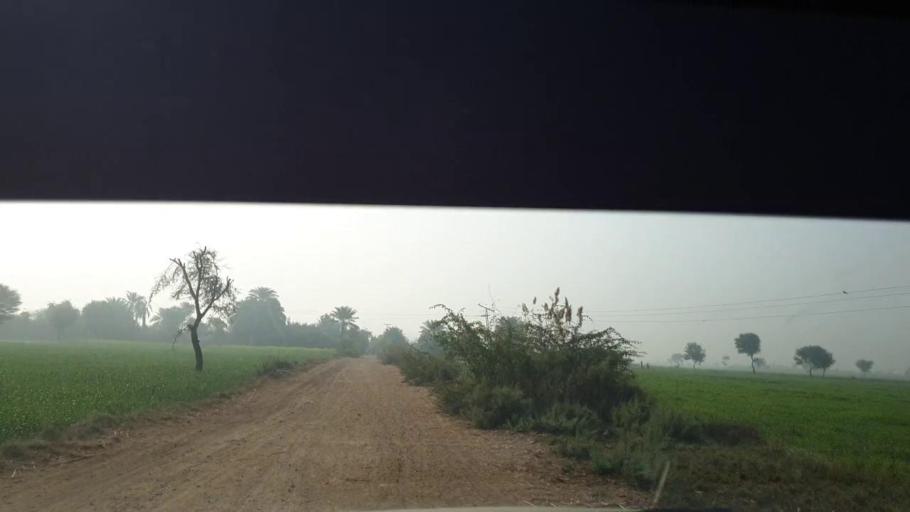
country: PK
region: Sindh
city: Berani
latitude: 25.7808
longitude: 68.7897
